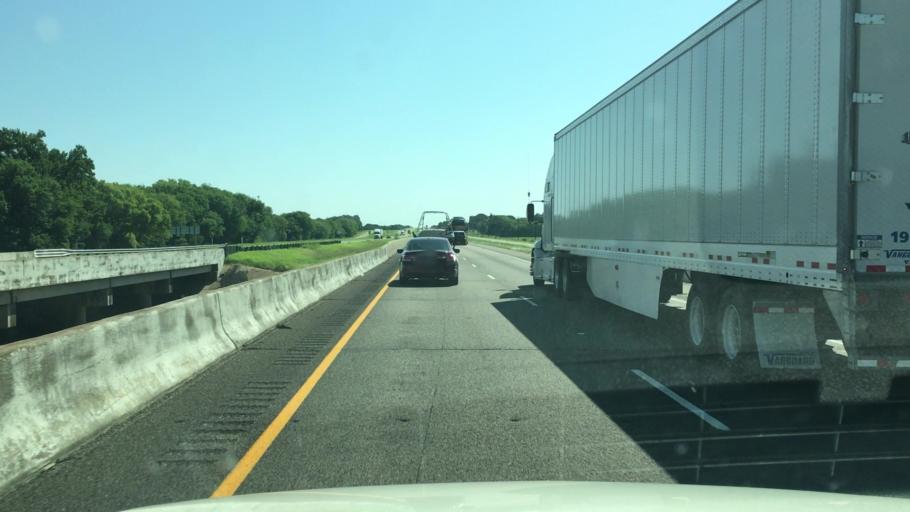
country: US
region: Texas
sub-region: Hopkins County
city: Sulphur Springs
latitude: 33.1497
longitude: -95.4415
